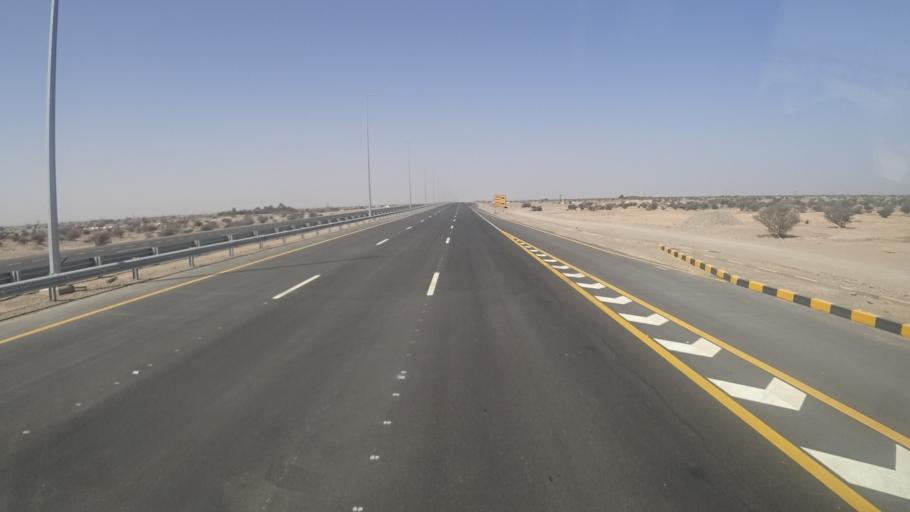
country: OM
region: Ash Sharqiyah
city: Sur
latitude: 22.2726
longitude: 59.2339
